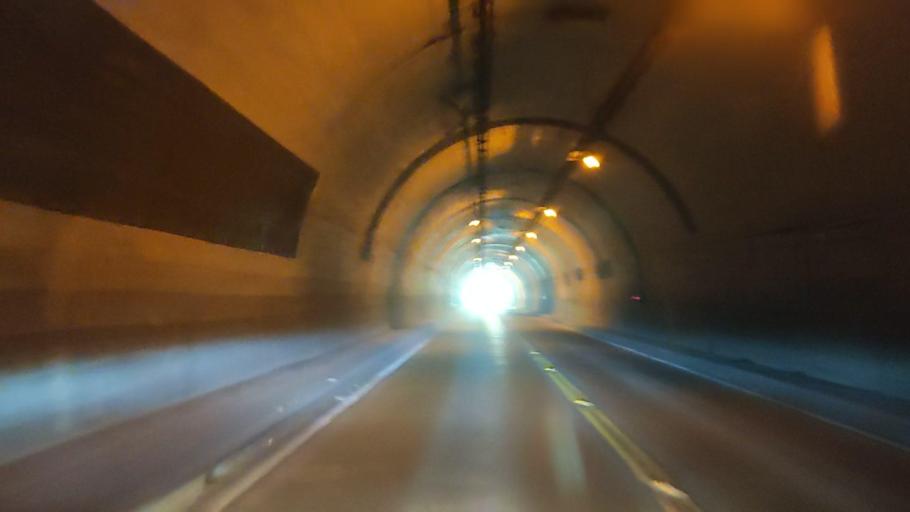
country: JP
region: Shizuoka
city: Ito
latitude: 34.9278
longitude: 139.0457
